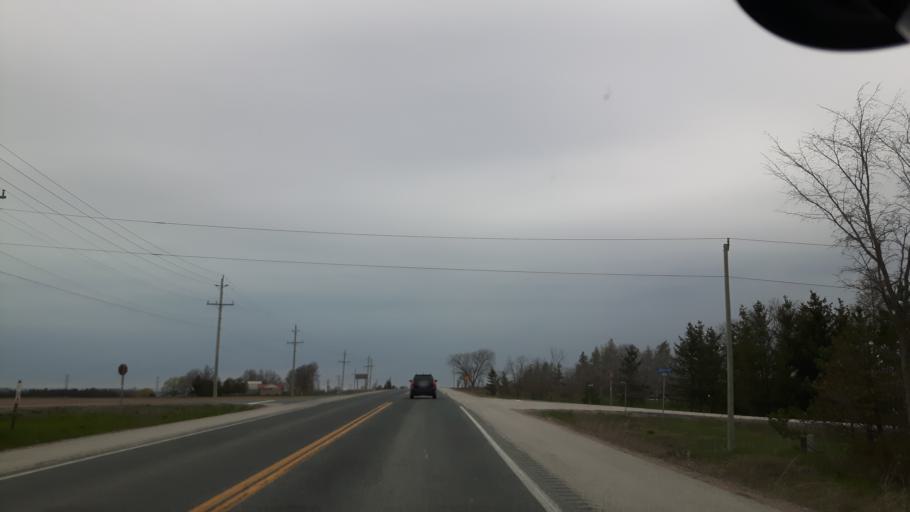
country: CA
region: Ontario
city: Goderich
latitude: 43.6923
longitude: -81.6350
